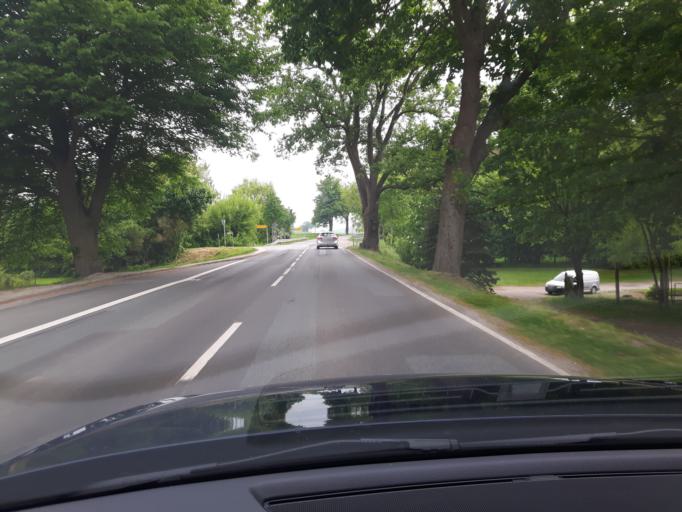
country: DE
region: Mecklenburg-Vorpommern
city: Teterow
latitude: 53.8291
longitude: 12.5666
